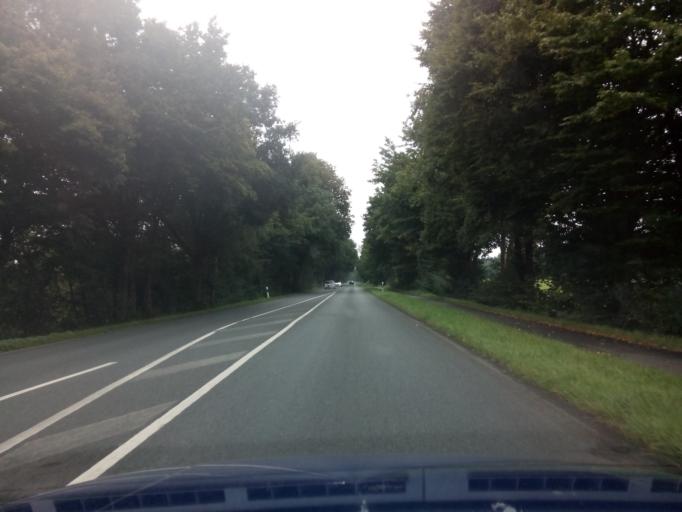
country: DE
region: Lower Saxony
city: Worpswede
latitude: 53.2351
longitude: 8.9481
